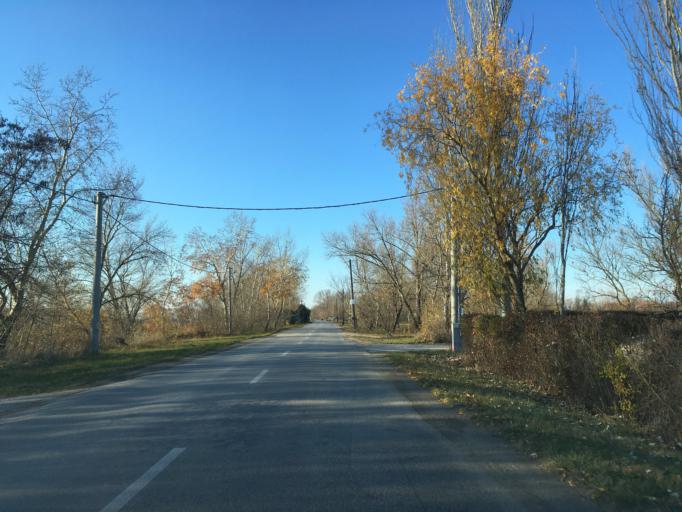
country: SK
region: Nitriansky
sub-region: Okres Komarno
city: Hurbanovo
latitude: 47.8907
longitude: 18.1965
